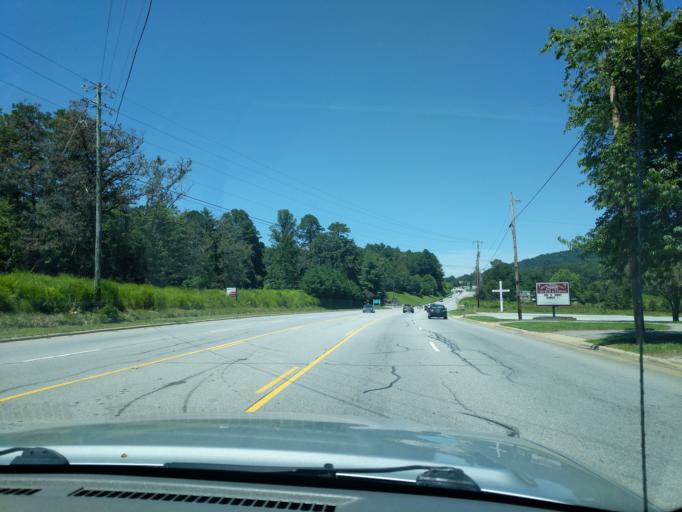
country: US
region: North Carolina
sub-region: Henderson County
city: Fletcher
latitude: 35.4524
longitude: -82.5099
